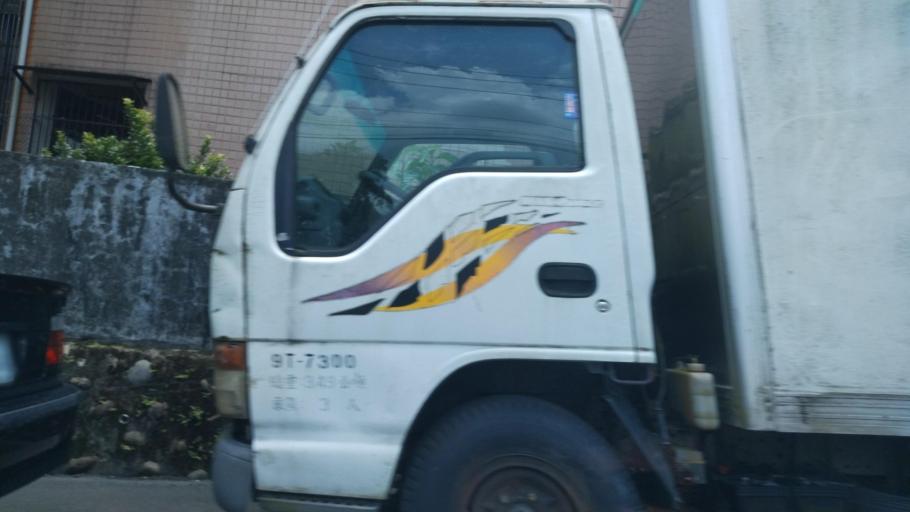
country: TW
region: Taipei
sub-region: Taipei
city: Banqiao
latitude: 24.9494
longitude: 121.4892
